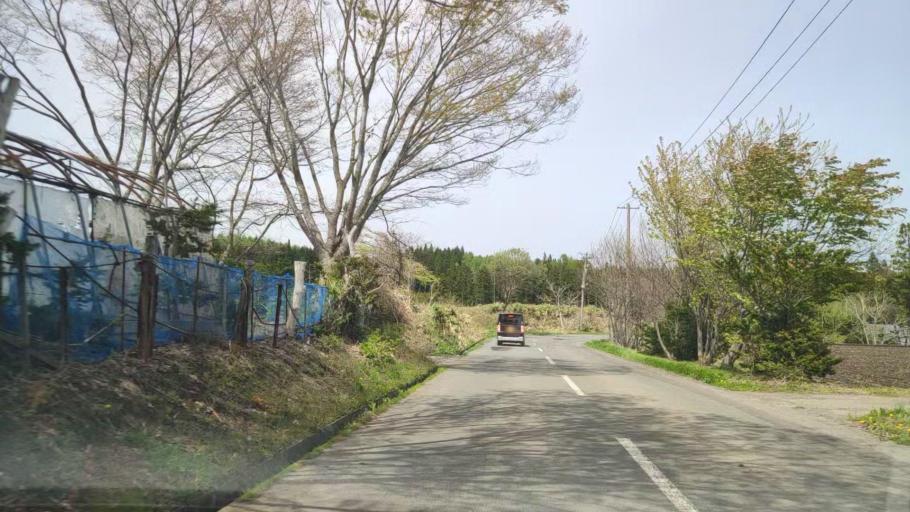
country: JP
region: Aomori
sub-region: Misawa Shi
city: Inuotose
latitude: 40.7650
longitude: 141.1189
